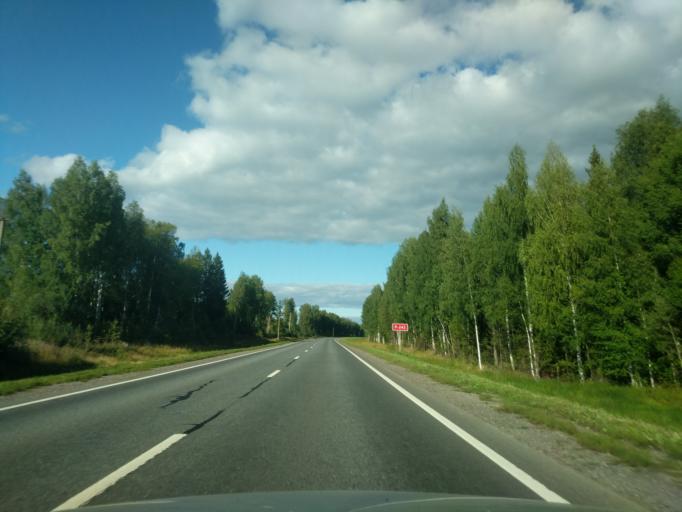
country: RU
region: Kostroma
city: Manturovo
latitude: 58.1520
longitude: 44.3759
